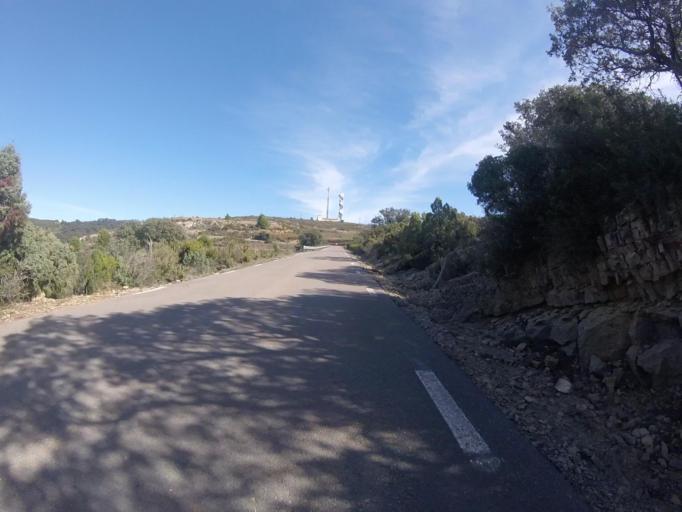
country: ES
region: Valencia
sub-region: Provincia de Castello
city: Sarratella
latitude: 40.2983
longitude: 0.0287
